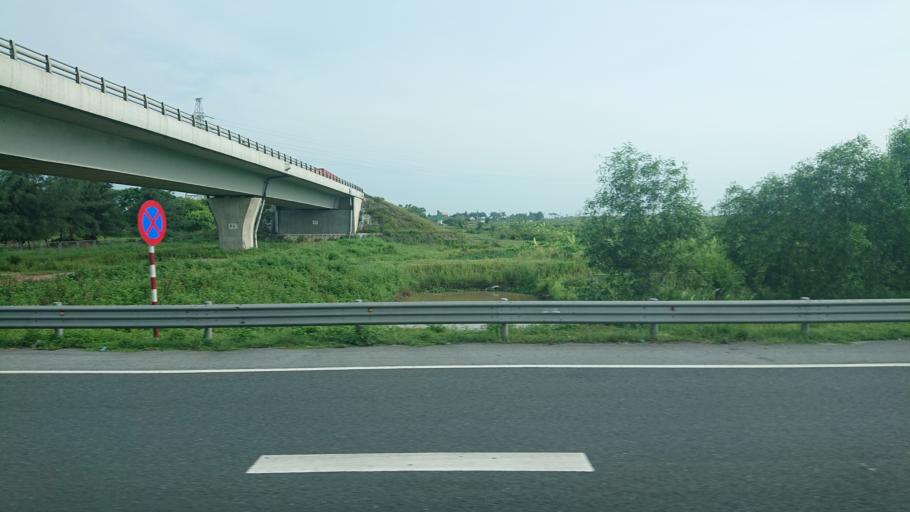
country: VN
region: Hai Phong
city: An Lao
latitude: 20.8026
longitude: 106.5269
